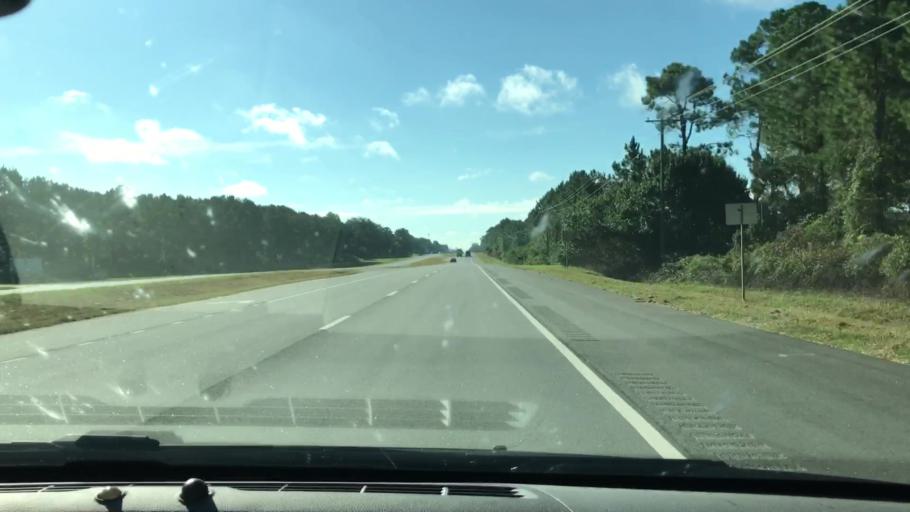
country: US
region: Georgia
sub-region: Lee County
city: Leesburg
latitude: 31.6739
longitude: -84.2922
